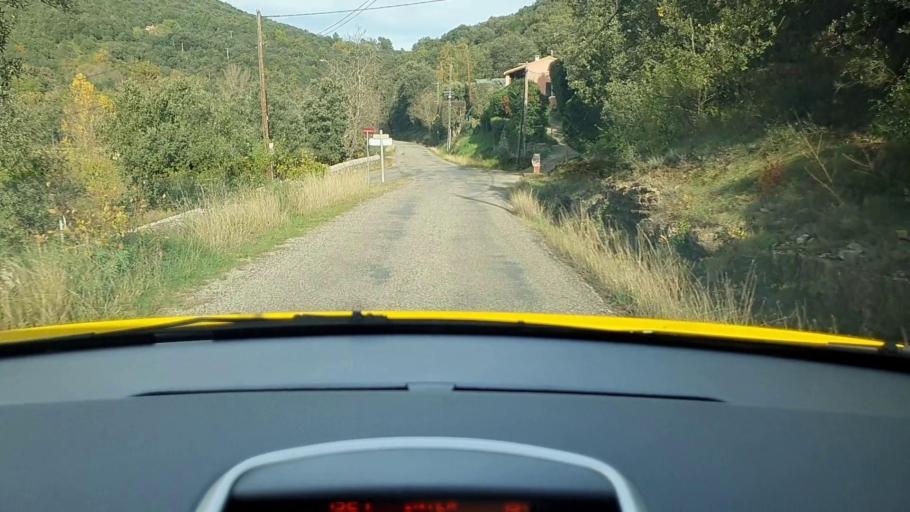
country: FR
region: Languedoc-Roussillon
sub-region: Departement du Gard
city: Saint-Jean-du-Gard
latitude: 44.0587
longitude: 3.9232
